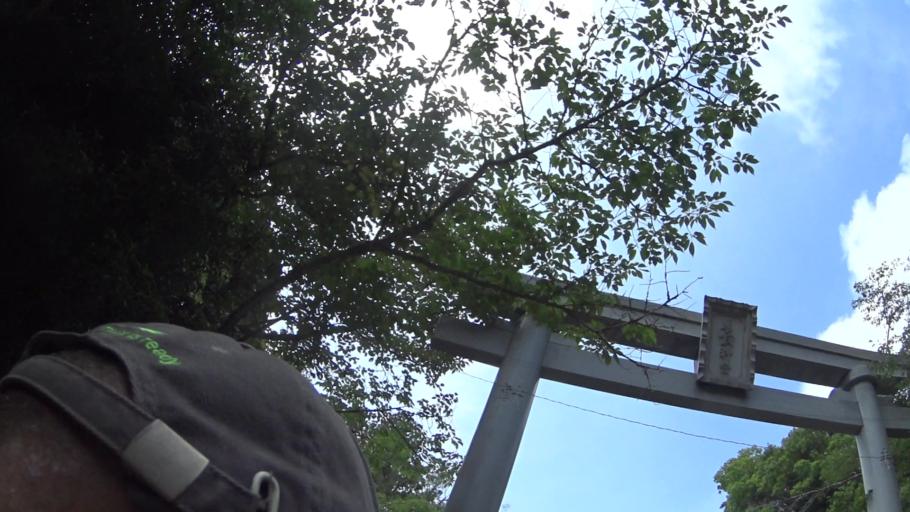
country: JP
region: Chiba
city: Sawara
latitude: 35.8850
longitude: 140.5288
